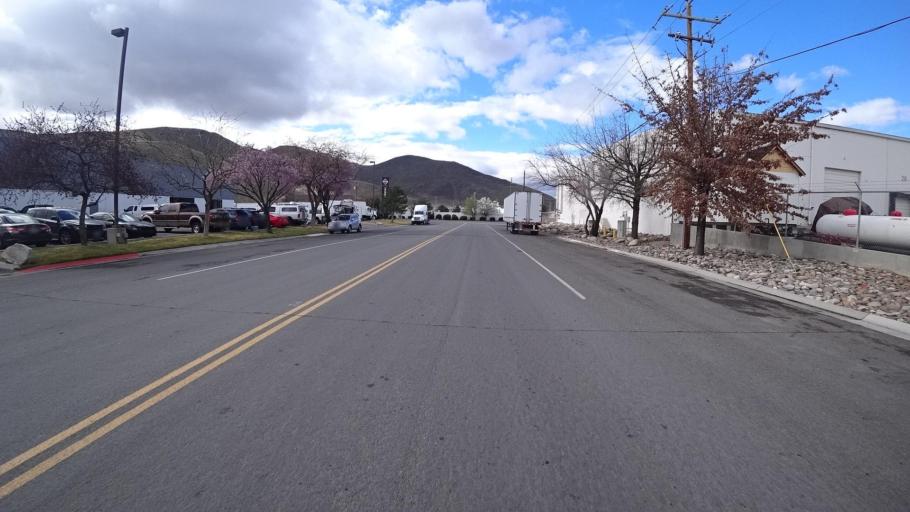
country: US
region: Nevada
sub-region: Washoe County
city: Sparks
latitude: 39.5227
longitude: -119.6985
